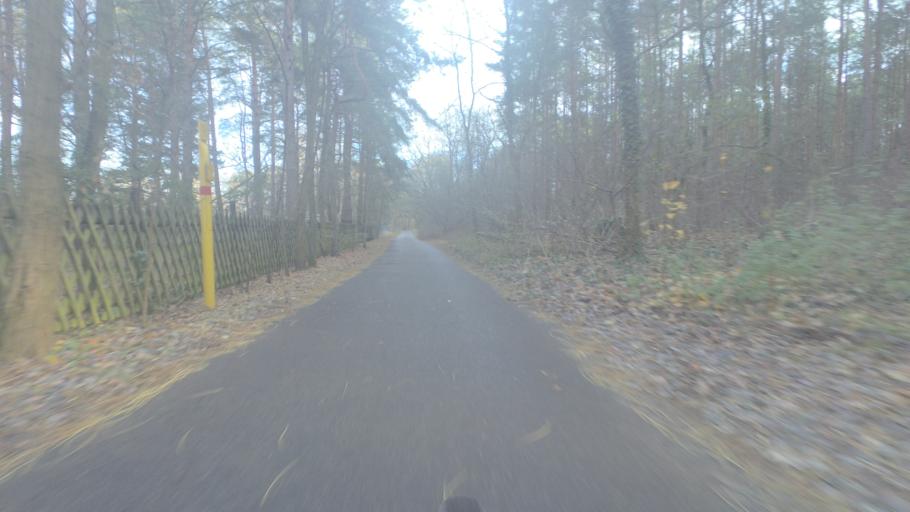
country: DE
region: Brandenburg
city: Zossen
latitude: 52.2201
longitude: 13.4849
